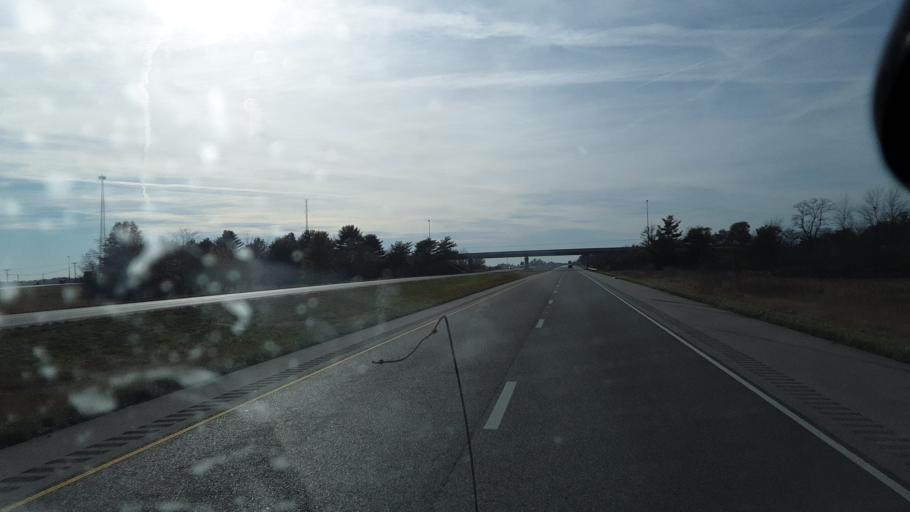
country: US
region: Illinois
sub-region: Fayette County
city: Saint Elmo
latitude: 39.0123
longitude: -88.8544
